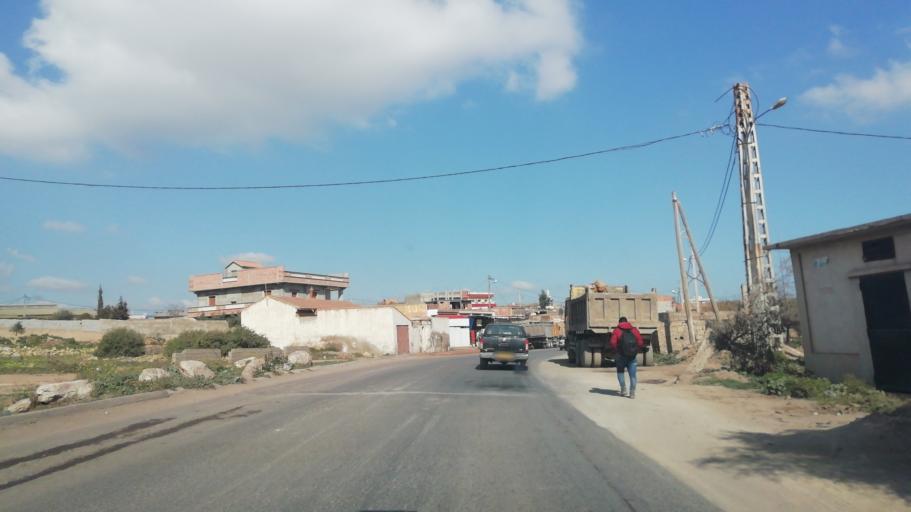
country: DZ
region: Oran
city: Ain el Bya
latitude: 35.7709
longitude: -0.2792
